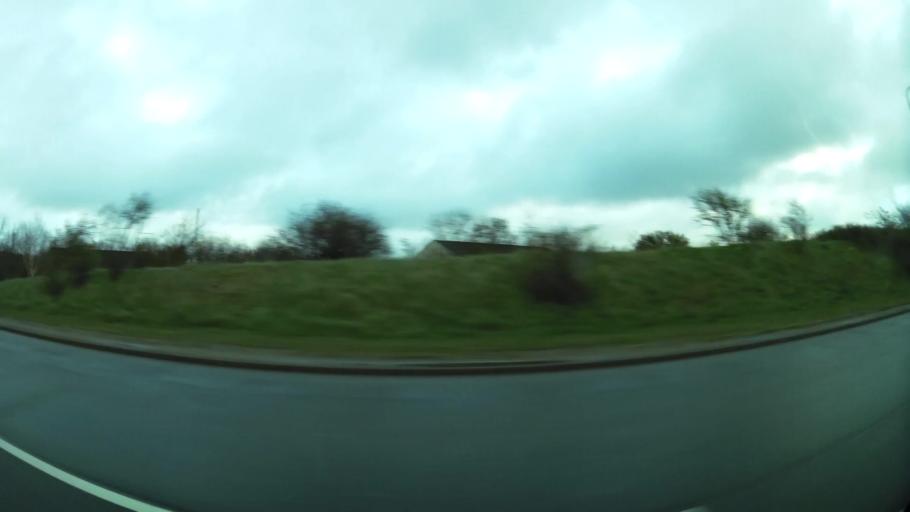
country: DK
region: Central Jutland
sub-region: Ringkobing-Skjern Kommune
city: Skjern
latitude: 55.9504
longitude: 8.4836
